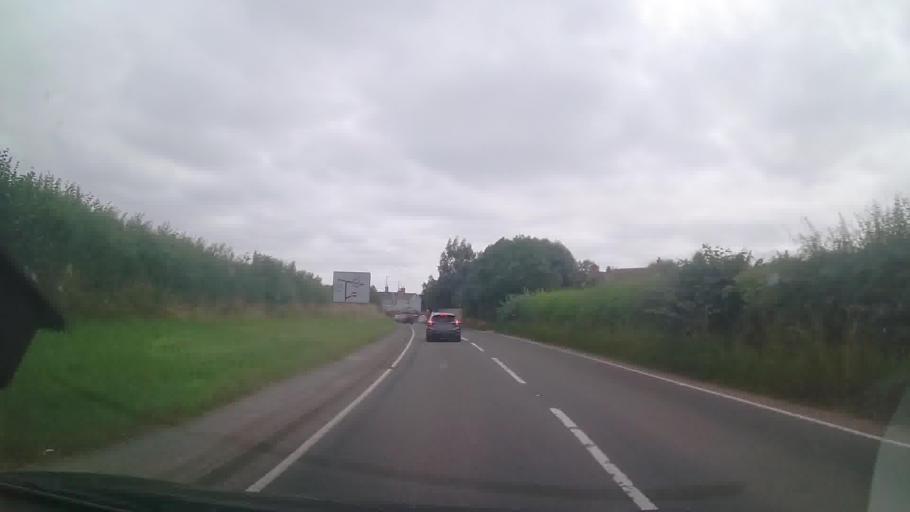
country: GB
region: England
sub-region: Leicestershire
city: Desford
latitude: 52.6352
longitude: -1.2797
